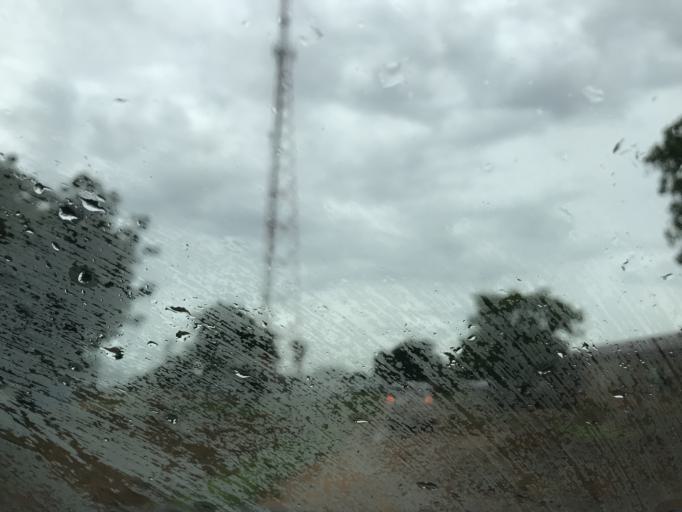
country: GH
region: Upper West
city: Wa
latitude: 10.5133
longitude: -2.6975
